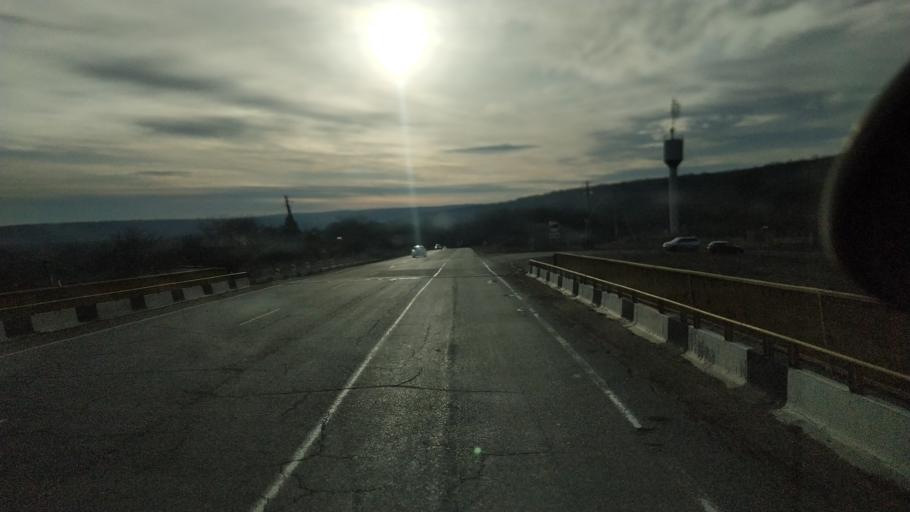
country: MD
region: Chisinau
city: Vadul lui Voda
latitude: 47.0852
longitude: 29.0767
